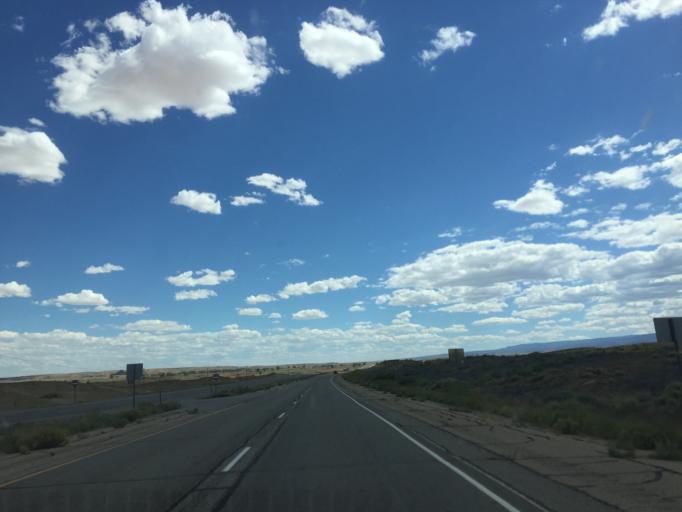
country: US
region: New Mexico
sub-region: San Juan County
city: Shiprock
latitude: 36.3246
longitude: -108.7099
